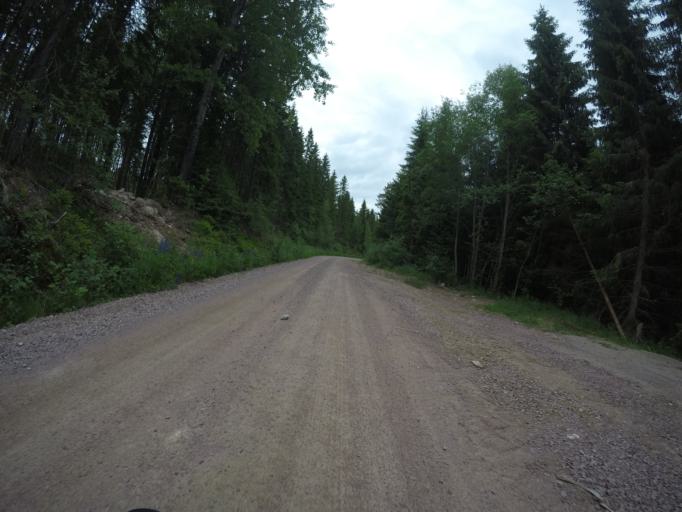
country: SE
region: Dalarna
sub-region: Ludvika Kommun
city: Abborrberget
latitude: 60.1065
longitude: 14.5195
